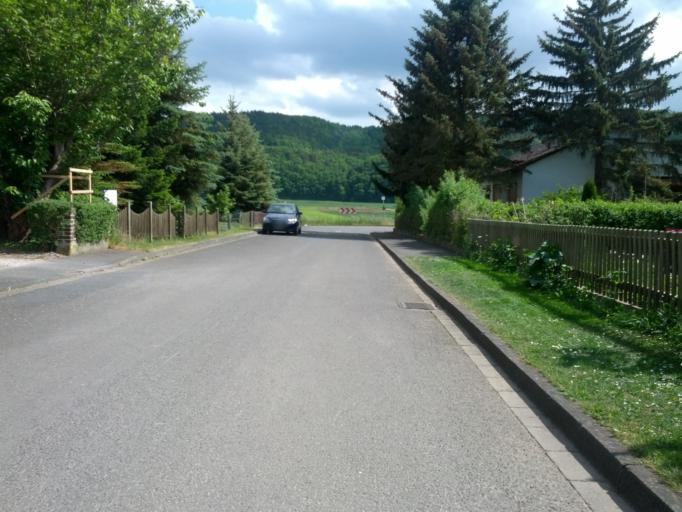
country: DE
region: Thuringia
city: Treffurt
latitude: 51.1276
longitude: 10.2007
